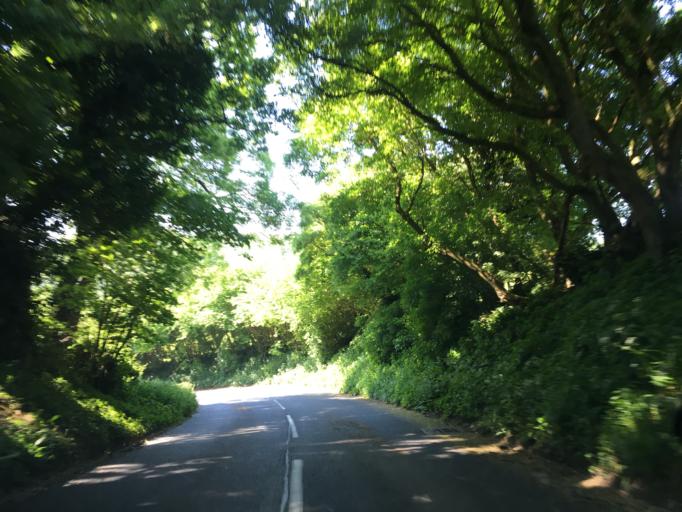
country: GB
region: England
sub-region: Isle of Wight
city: Newchurch
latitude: 50.6828
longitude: -1.2014
